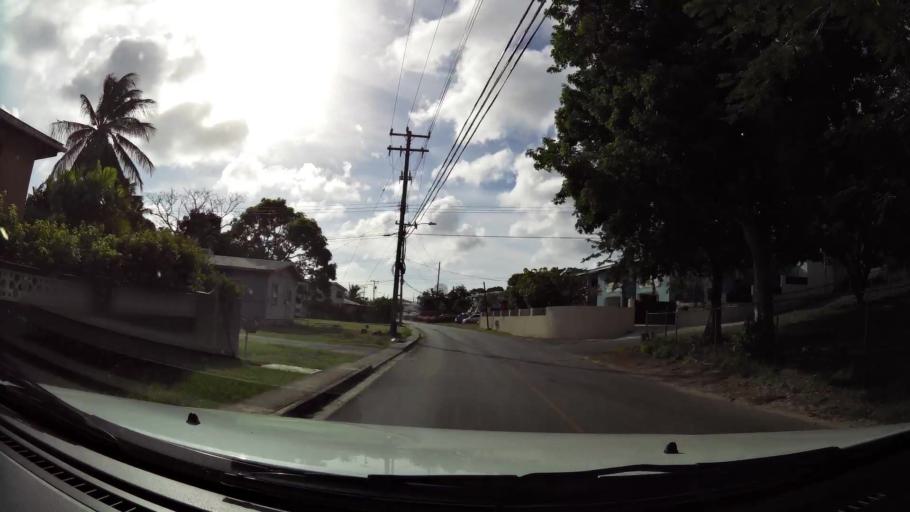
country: BB
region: Saint Michael
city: Bridgetown
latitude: 13.0782
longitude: -59.5891
